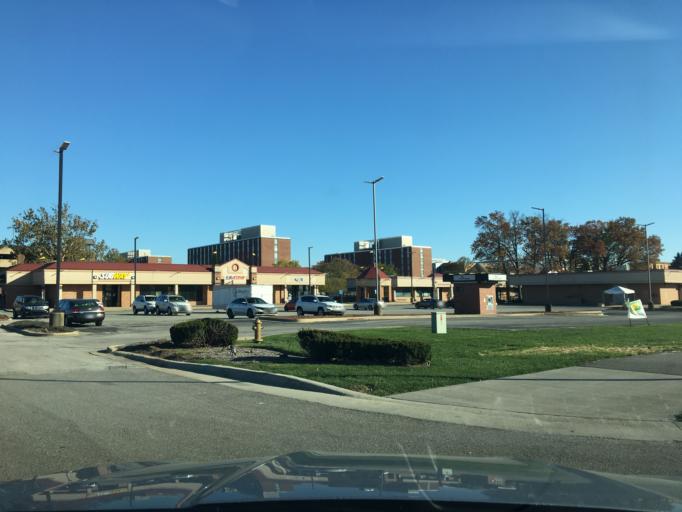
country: US
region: Indiana
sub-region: Tippecanoe County
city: West Lafayette
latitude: 40.4263
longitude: -86.9305
